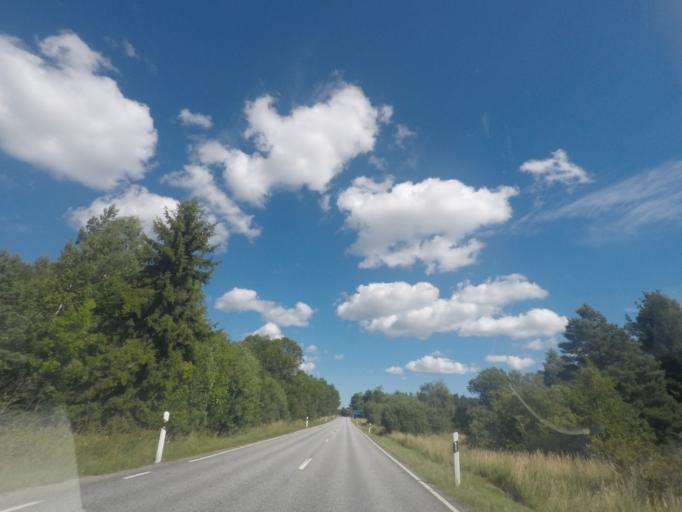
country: SE
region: Stockholm
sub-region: Norrtalje Kommun
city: Hallstavik
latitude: 59.9471
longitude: 18.7574
